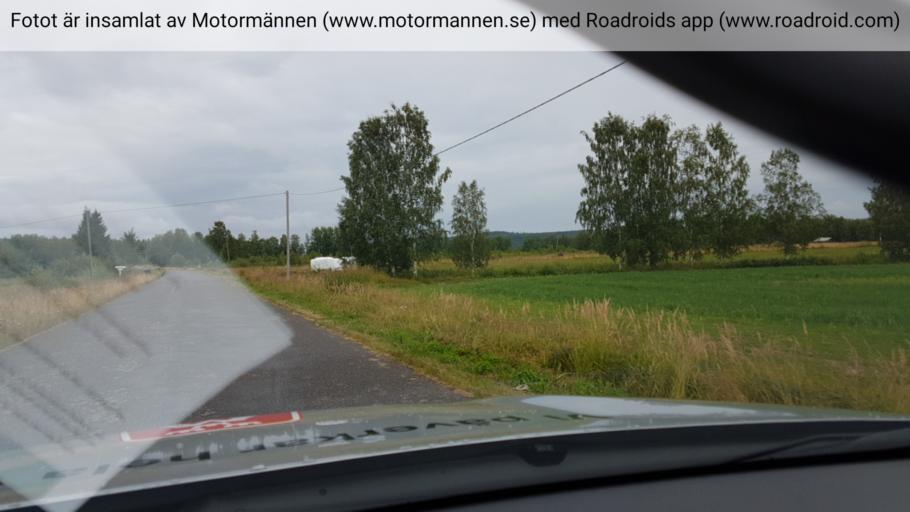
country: SE
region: Norrbotten
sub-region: Alvsbyns Kommun
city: AElvsbyn
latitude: 66.0452
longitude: 20.9813
